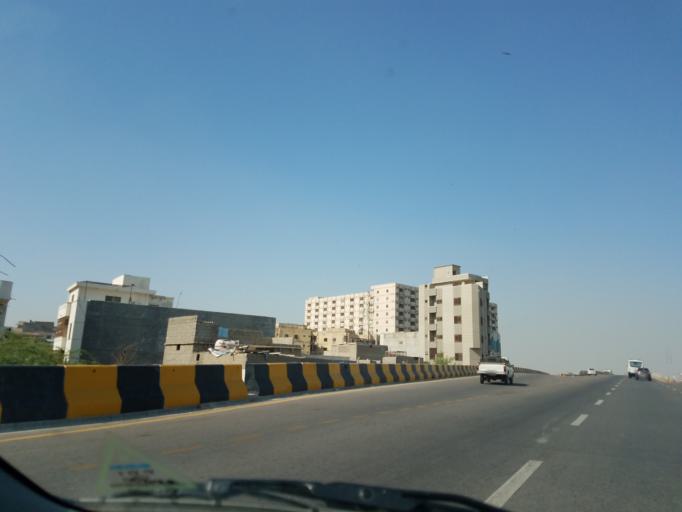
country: PK
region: Sindh
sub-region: Karachi District
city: Karachi
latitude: 24.9047
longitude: 67.0627
